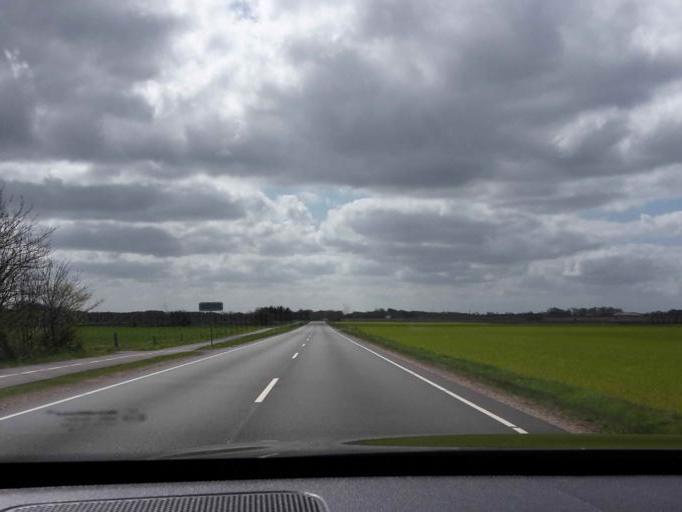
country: DK
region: South Denmark
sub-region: Varde Kommune
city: Olgod
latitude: 55.7461
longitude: 8.6193
